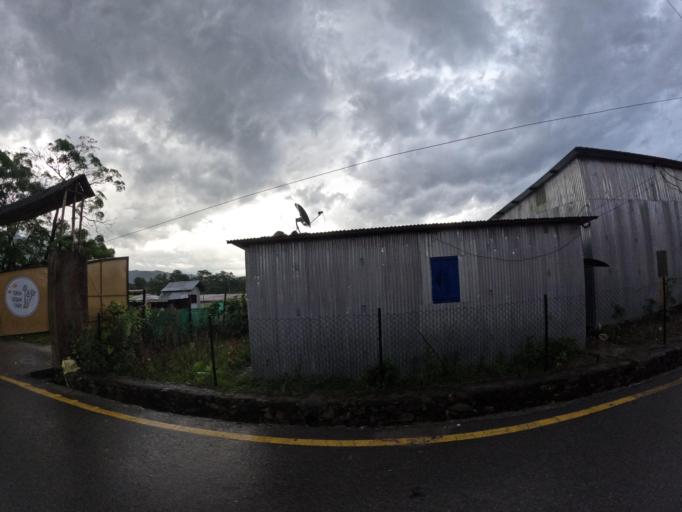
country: NP
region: Central Region
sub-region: Bagmati Zone
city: Kathmandu
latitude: 27.7720
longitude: 85.3350
